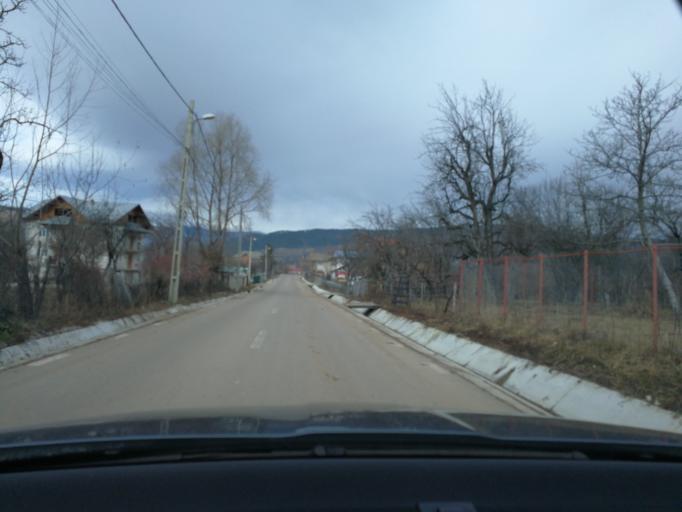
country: RO
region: Dambovita
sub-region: Comuna Buciumeni
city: Buciumeni
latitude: 45.1458
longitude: 25.4554
